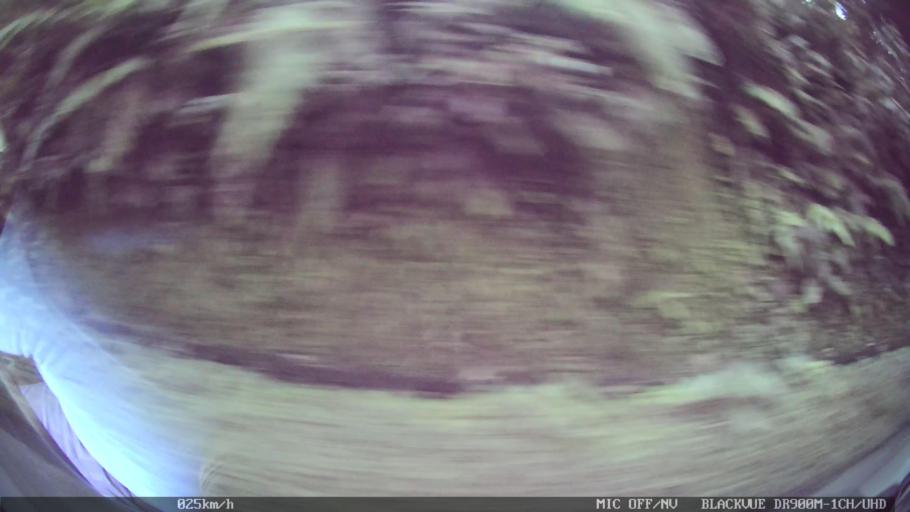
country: ID
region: Bali
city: Peneng
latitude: -8.3639
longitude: 115.2196
